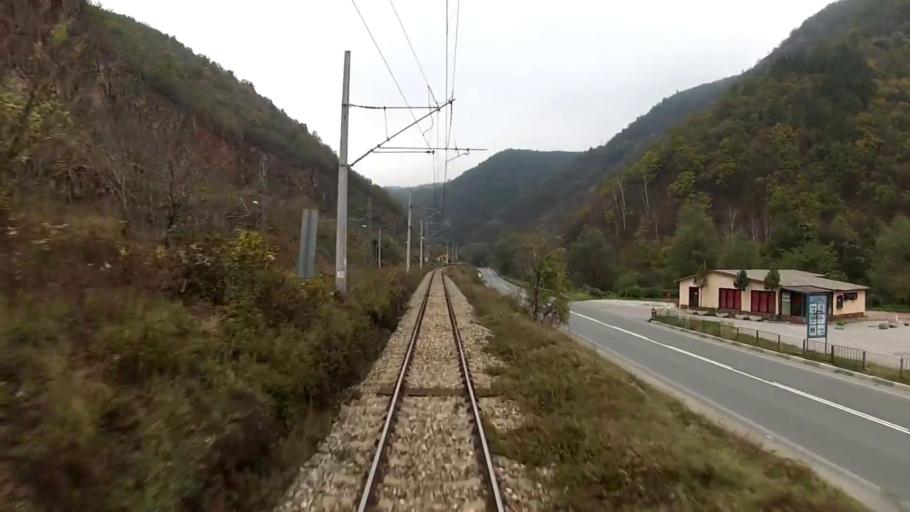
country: RS
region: Central Serbia
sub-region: Pirotski Okrug
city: Dimitrovgrad
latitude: 42.9749
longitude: 22.8494
